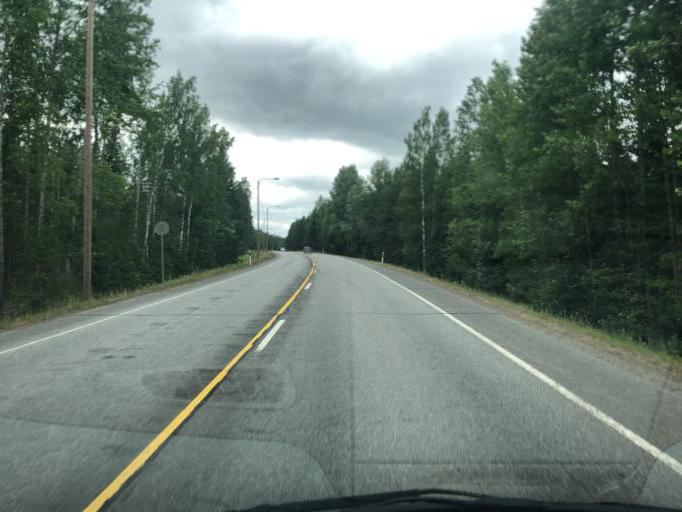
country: FI
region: Kymenlaakso
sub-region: Kouvola
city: Kouvola
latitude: 60.8933
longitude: 26.7574
